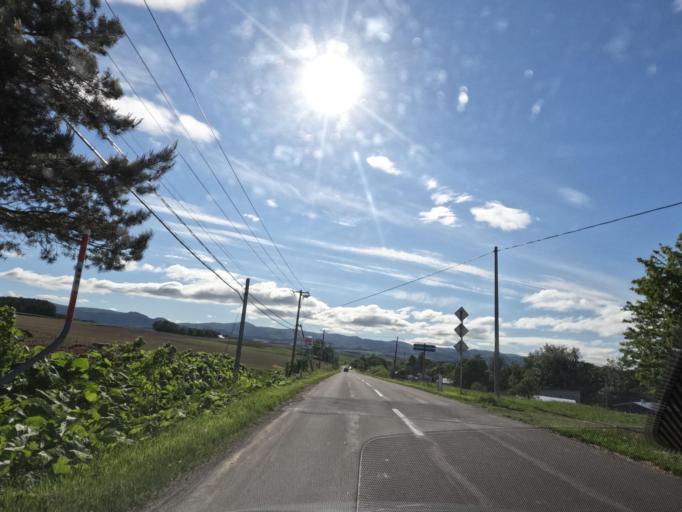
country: JP
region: Hokkaido
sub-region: Asahikawa-shi
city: Asahikawa
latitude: 43.5958
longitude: 142.4469
